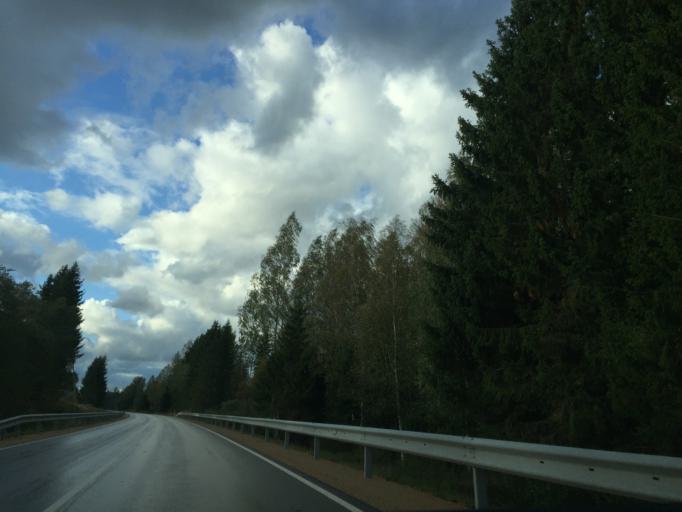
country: LV
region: Ligatne
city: Ligatne
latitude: 57.1537
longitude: 25.0695
